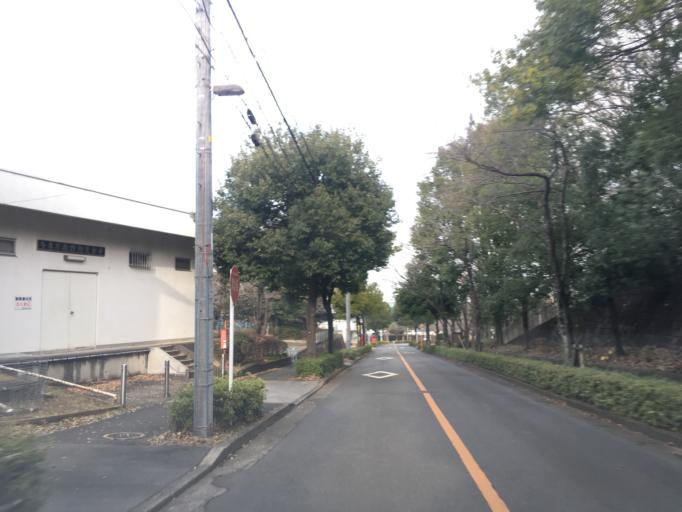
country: JP
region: Tokyo
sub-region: Machida-shi
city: Machida
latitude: 35.6078
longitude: 139.4345
